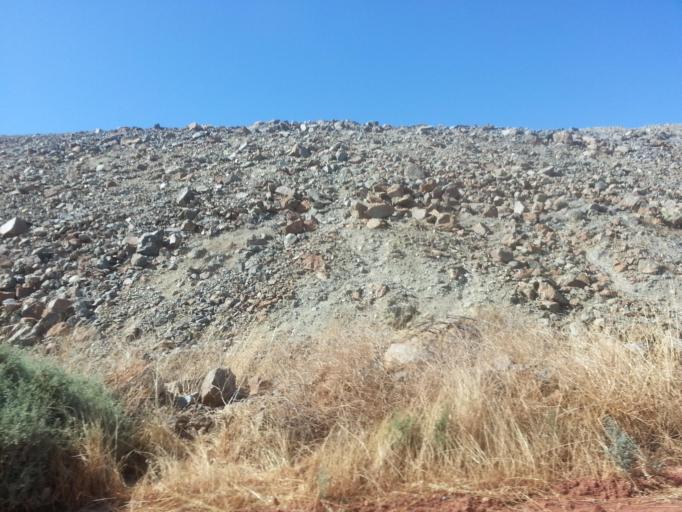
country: AU
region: Western Australia
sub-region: Irwin
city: Dongara
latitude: -29.4960
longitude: 115.8615
